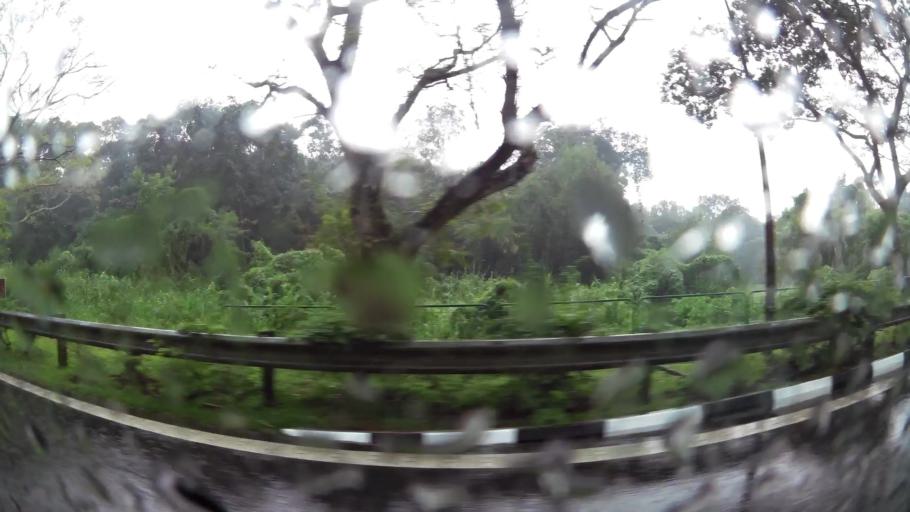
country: MY
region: Johor
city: Johor Bahru
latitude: 1.3936
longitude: 103.8202
